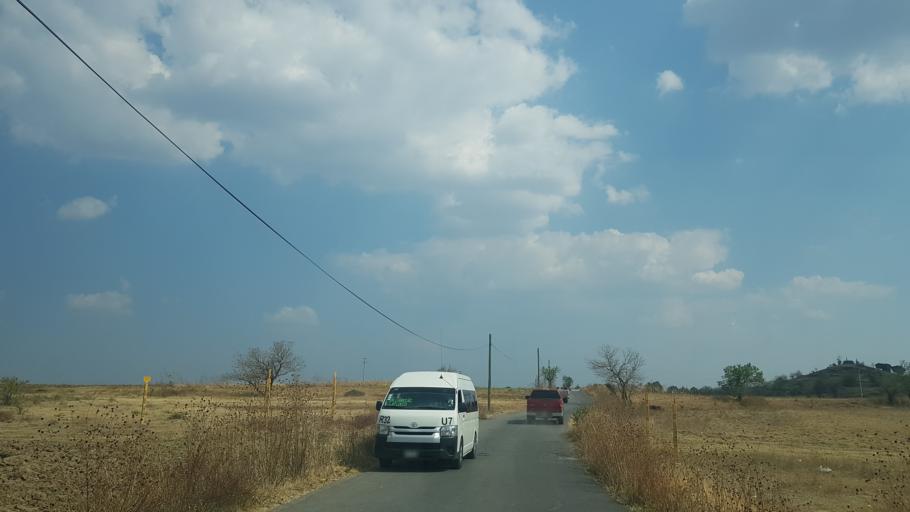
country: MX
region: Puebla
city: San Juan Amecac
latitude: 18.8200
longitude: -98.6530
